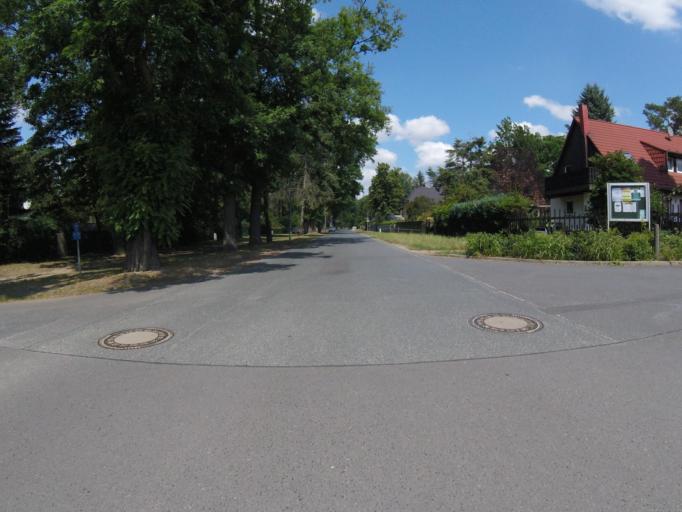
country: DE
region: Brandenburg
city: Bestensee
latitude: 52.2769
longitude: 13.6574
